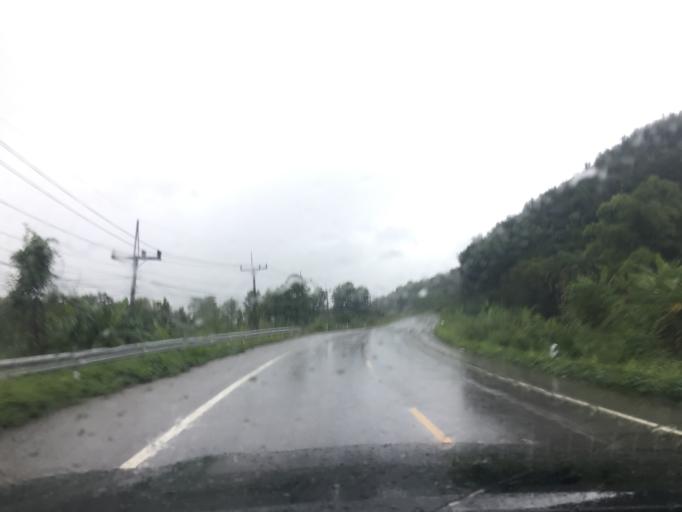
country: TH
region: Chiang Rai
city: Chiang Saen
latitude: 20.2734
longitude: 100.1995
